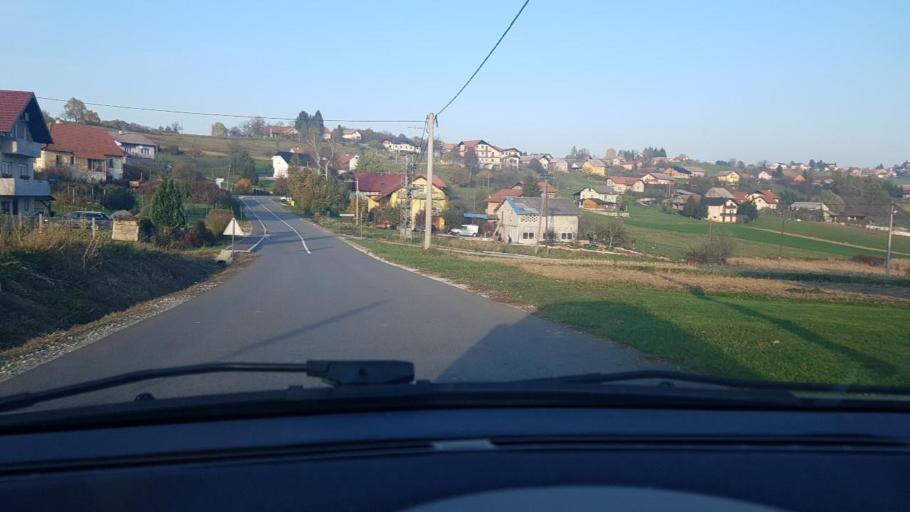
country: SI
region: Rogaska Slatina
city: Rogaska Slatina
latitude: 46.2115
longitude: 15.6516
